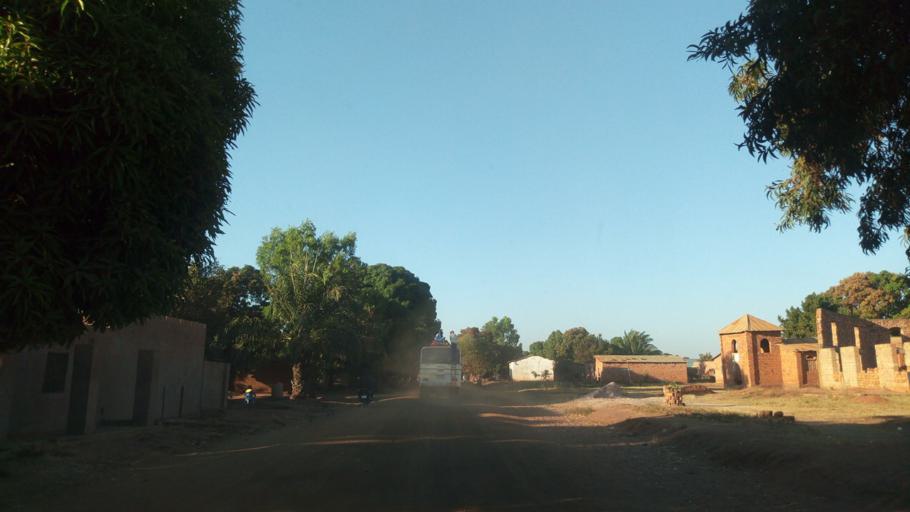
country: ZM
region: Luapula
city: Mwense
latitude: -10.3800
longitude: 28.6141
